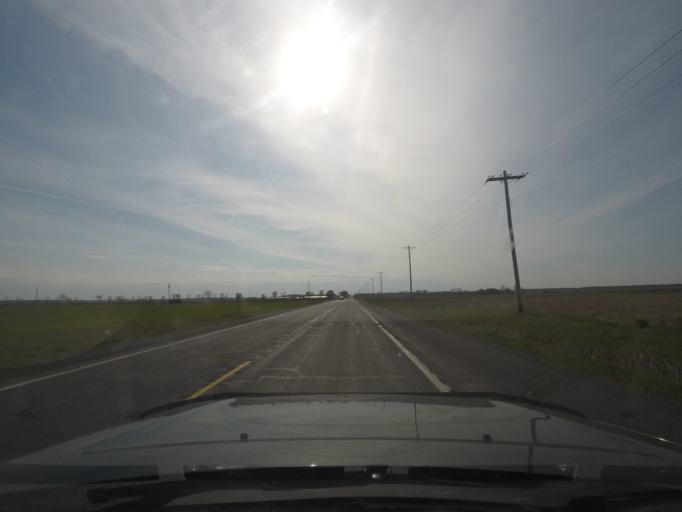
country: US
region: Michigan
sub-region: Berrien County
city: Three Oaks
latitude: 41.7982
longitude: -86.5410
